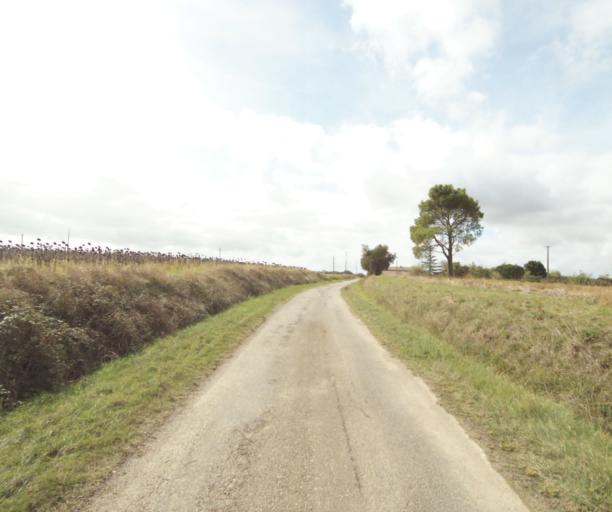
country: FR
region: Midi-Pyrenees
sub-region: Departement du Tarn-et-Garonne
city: Finhan
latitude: 43.8843
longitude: 1.1209
